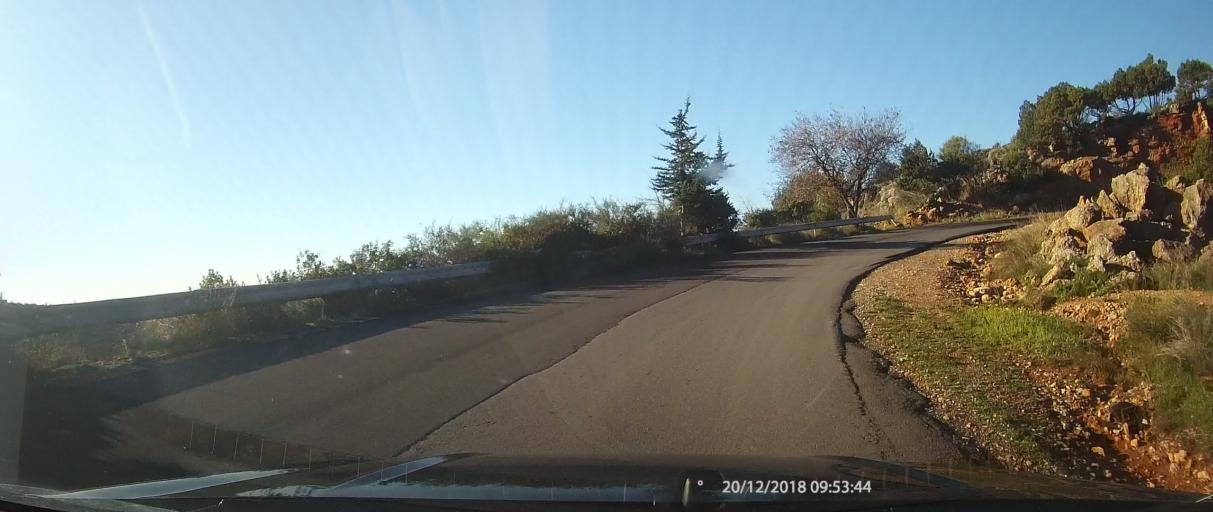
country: GR
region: Peloponnese
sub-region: Nomos Lakonias
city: Yerakion
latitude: 37.0109
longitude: 22.6376
